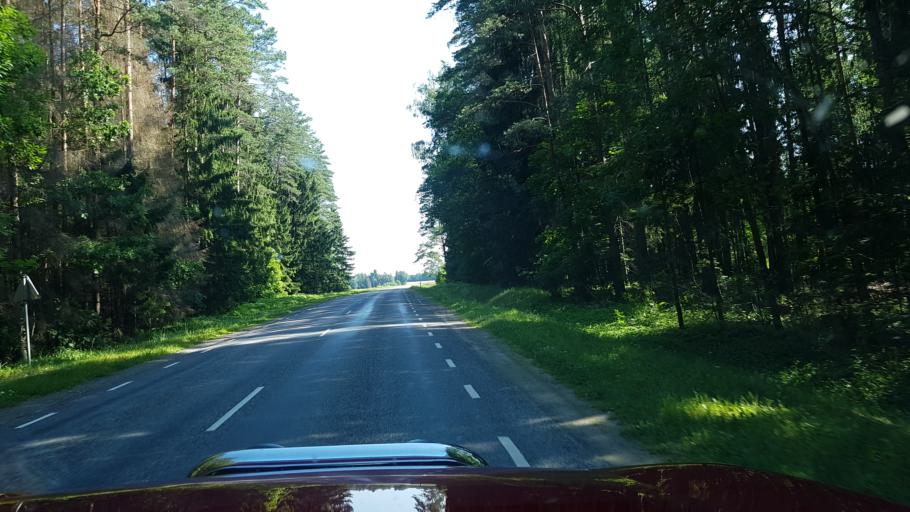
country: EE
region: Polvamaa
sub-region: Polva linn
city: Polva
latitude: 57.9953
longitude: 26.9093
